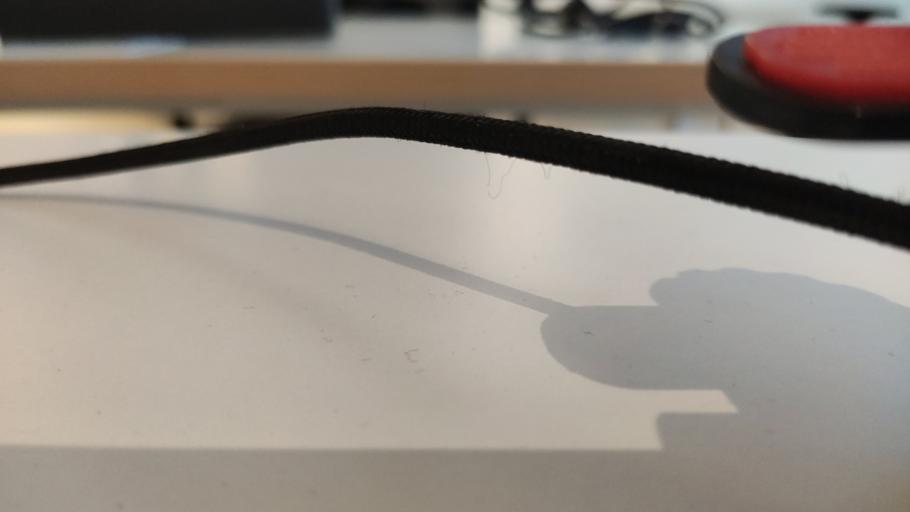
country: RU
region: Moskovskaya
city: Novopetrovskoye
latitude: 55.8698
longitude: 36.3978
